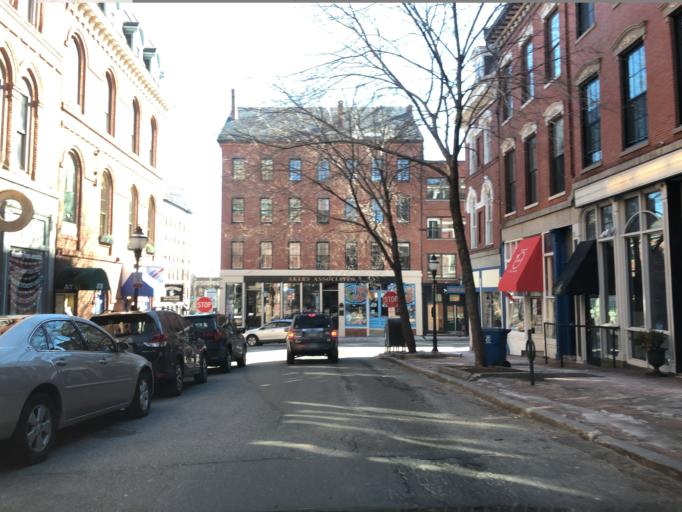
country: US
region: Maine
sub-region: Cumberland County
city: Portland
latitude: 43.6567
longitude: -70.2537
